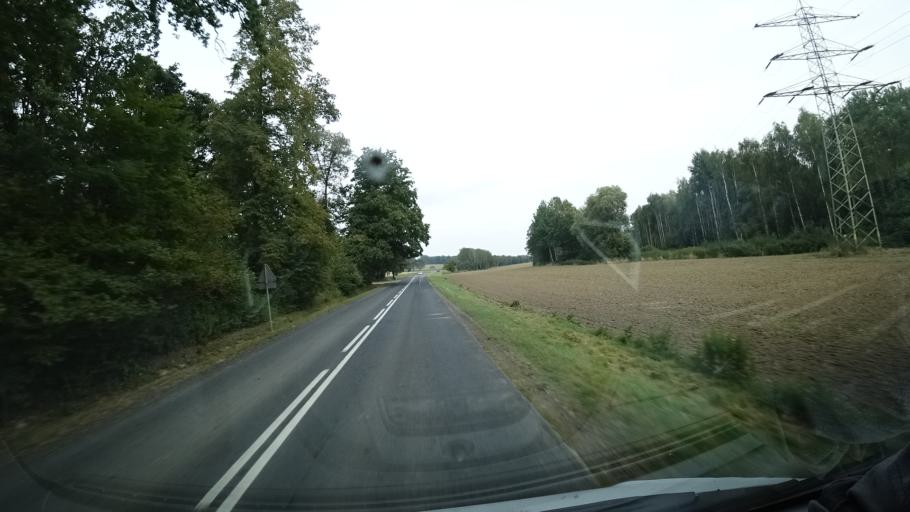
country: PL
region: Silesian Voivodeship
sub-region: Powiat gliwicki
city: Rudziniec
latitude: 50.3955
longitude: 18.4505
